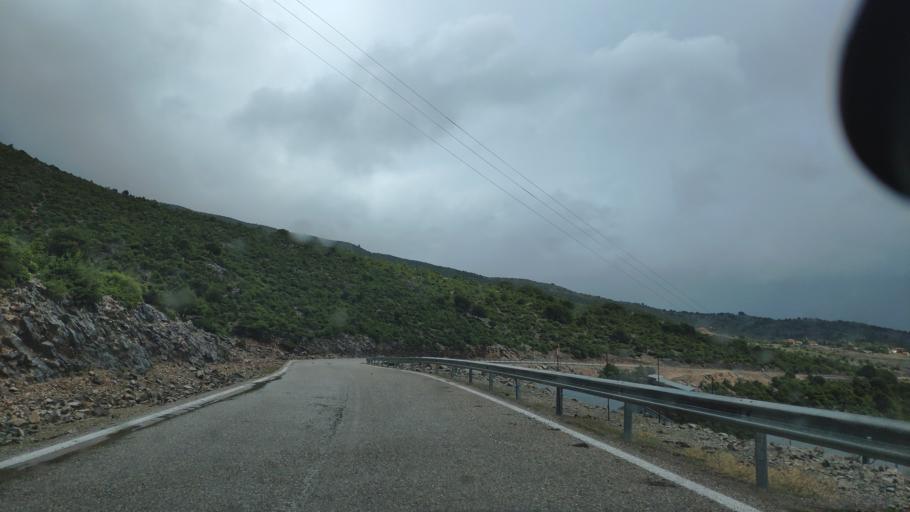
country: GR
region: West Greece
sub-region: Nomos Aitolias kai Akarnanias
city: Krikellos
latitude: 39.0701
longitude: 21.3842
